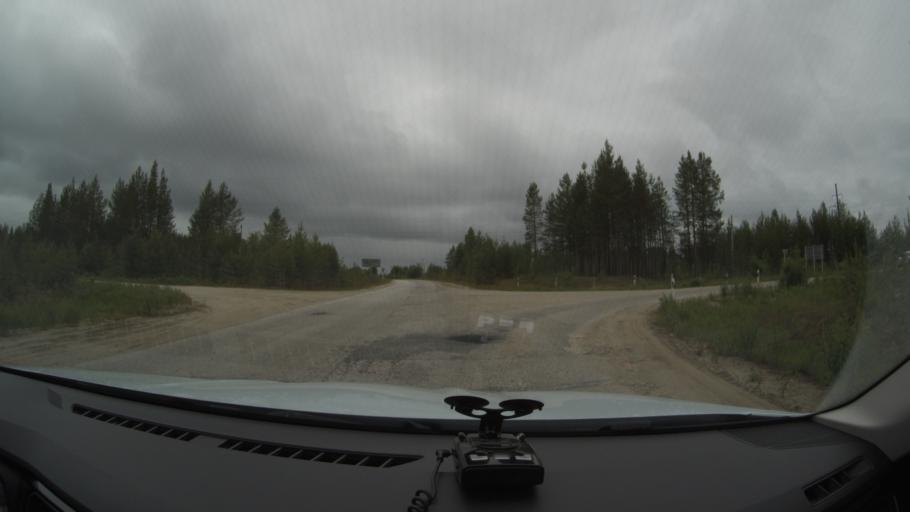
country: RU
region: Komi Republic
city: Kozhva
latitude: 65.1112
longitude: 57.0043
